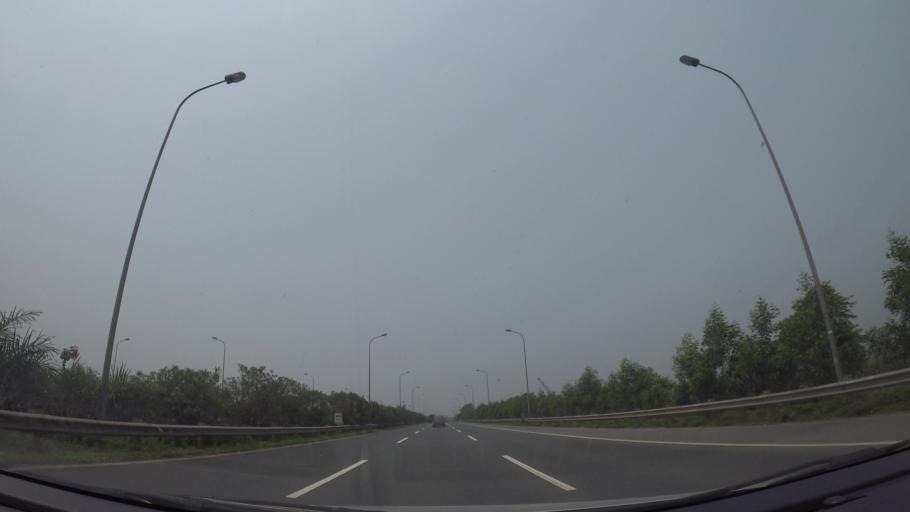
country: VN
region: Ha Noi
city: Quoc Oai
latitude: 20.9923
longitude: 105.5836
